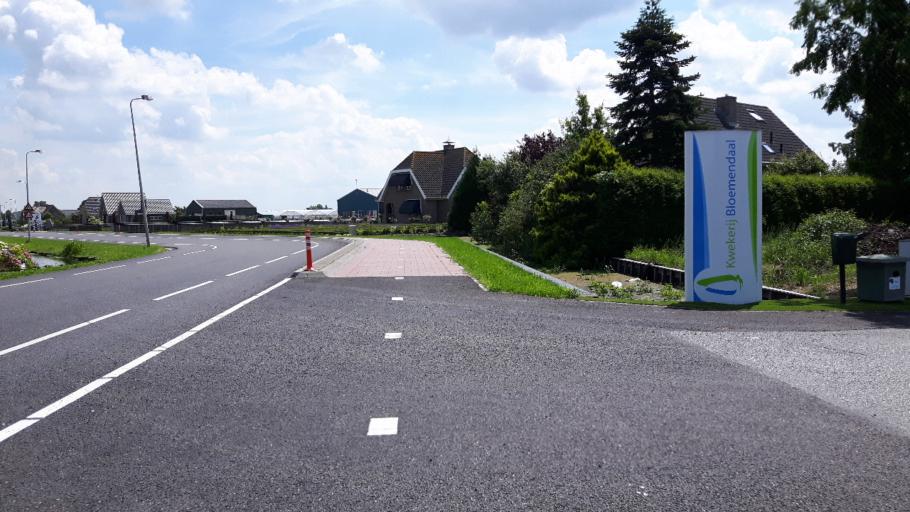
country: NL
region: South Holland
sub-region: Gemeente Boskoop
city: Boskoop
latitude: 52.0904
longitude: 4.6962
